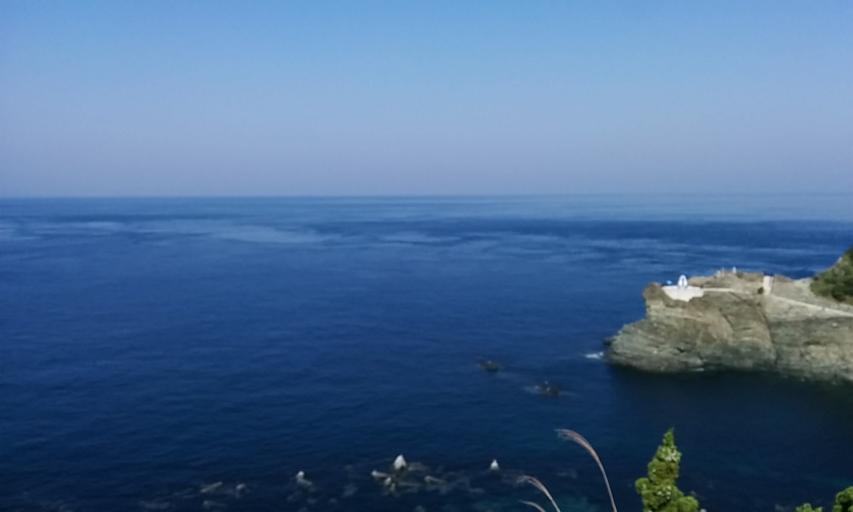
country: JP
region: Oita
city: Tsukumiura
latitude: 33.3398
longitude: 132.0248
